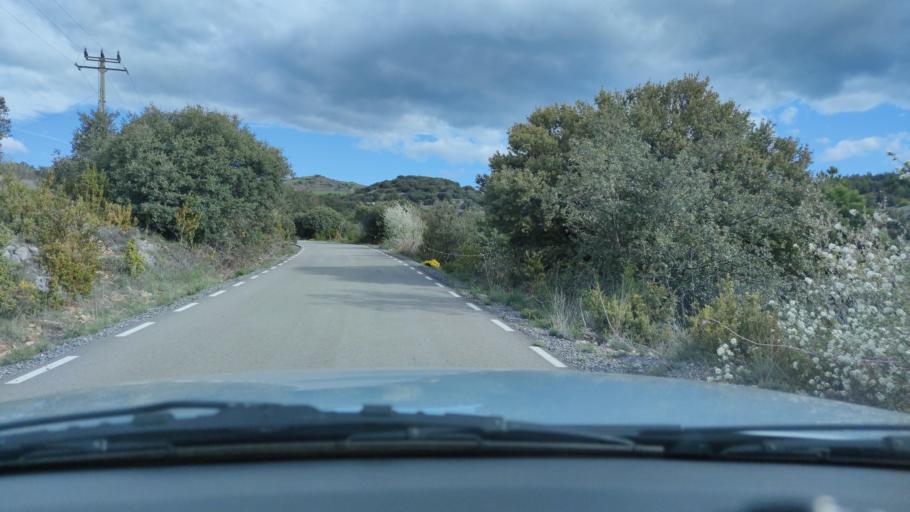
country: ES
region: Catalonia
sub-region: Provincia de Lleida
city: Coll de Nargo
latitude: 42.2308
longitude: 1.4048
